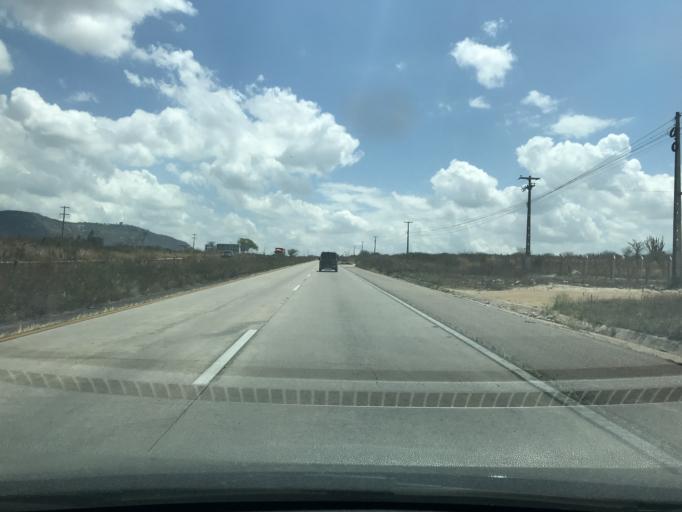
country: BR
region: Pernambuco
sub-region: Bezerros
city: Bezerros
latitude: -8.2915
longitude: -35.8233
